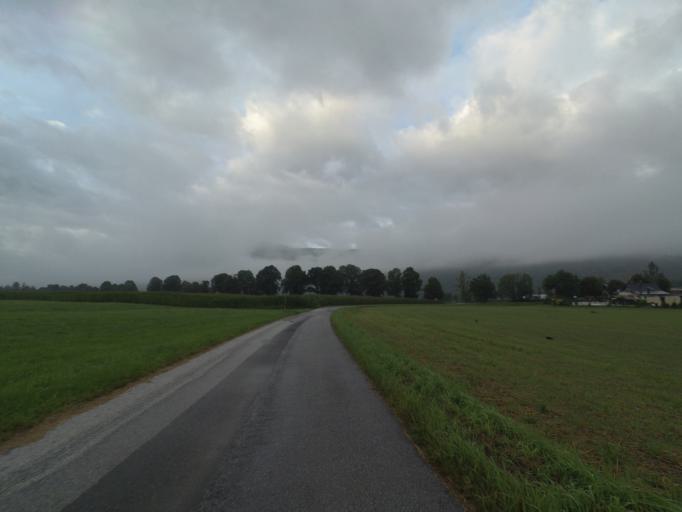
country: AT
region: Salzburg
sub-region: Politischer Bezirk Hallein
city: Puch bei Hallein
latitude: 47.7191
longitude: 13.0727
